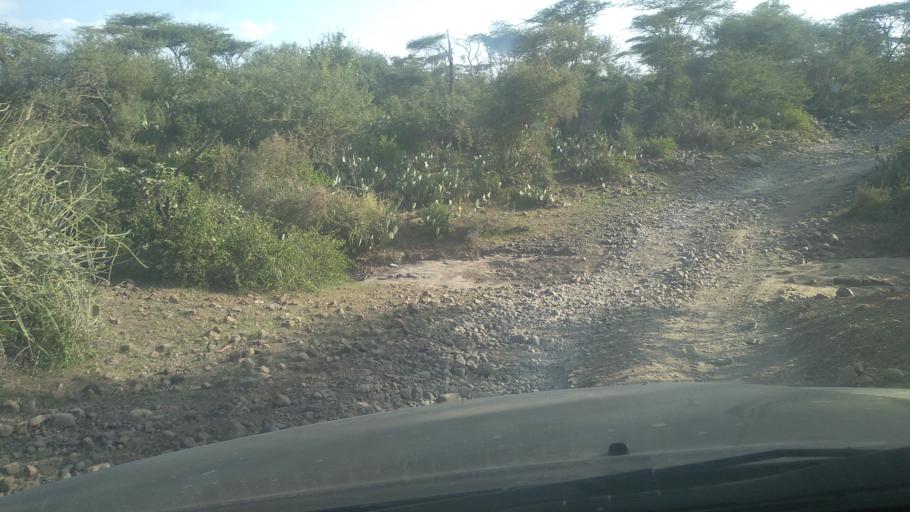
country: ET
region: Oromiya
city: Hirna
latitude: 9.4063
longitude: 40.9557
